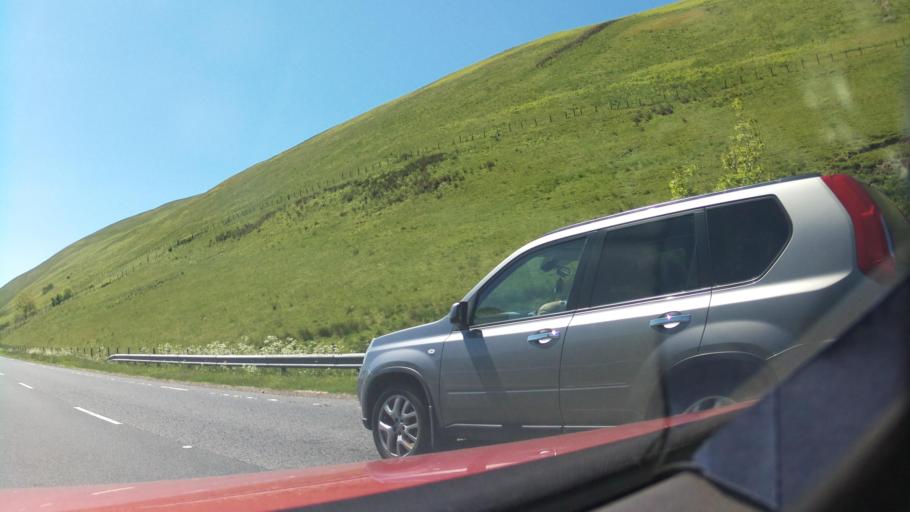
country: GB
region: Scotland
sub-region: Dumfries and Galloway
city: Langholm
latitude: 55.2432
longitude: -2.9698
